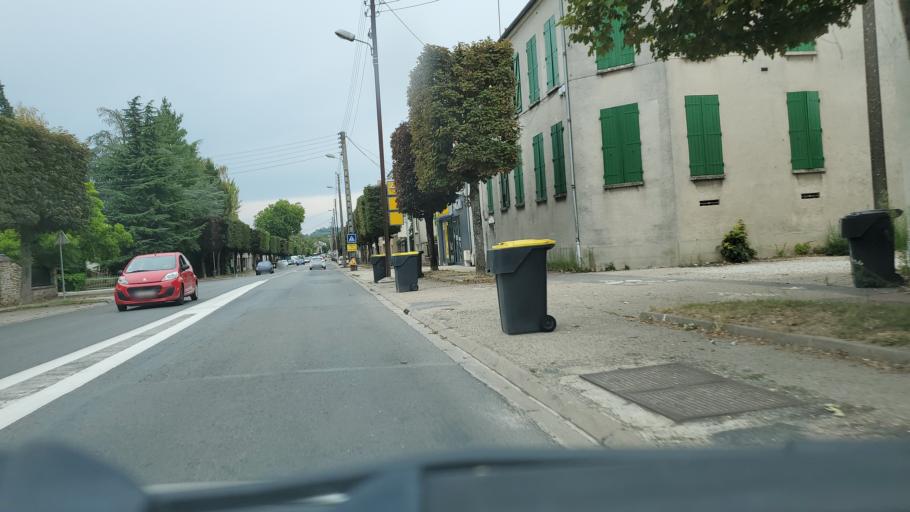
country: FR
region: Ile-de-France
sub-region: Departement de Seine-et-Marne
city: Coulommiers
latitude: 48.8042
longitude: 3.0852
